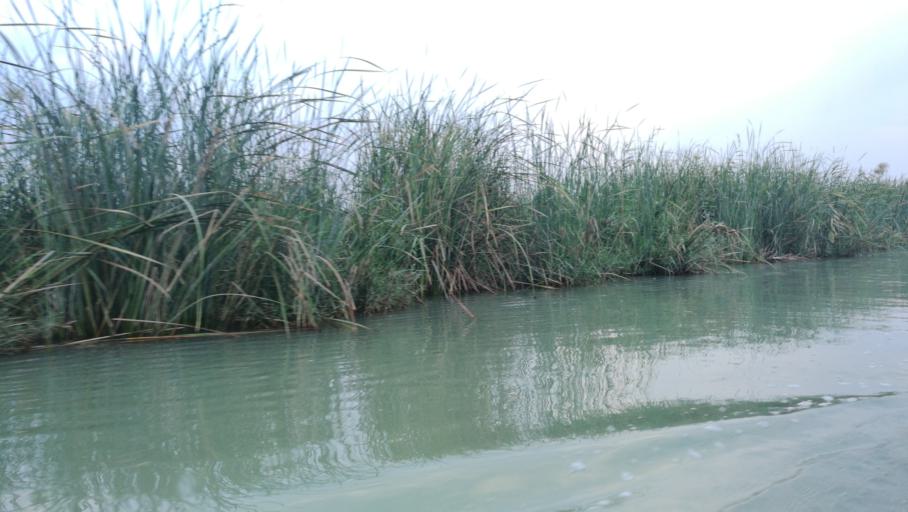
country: IQ
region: Dhi Qar
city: Al Jabayish
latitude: 30.9806
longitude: 47.0416
